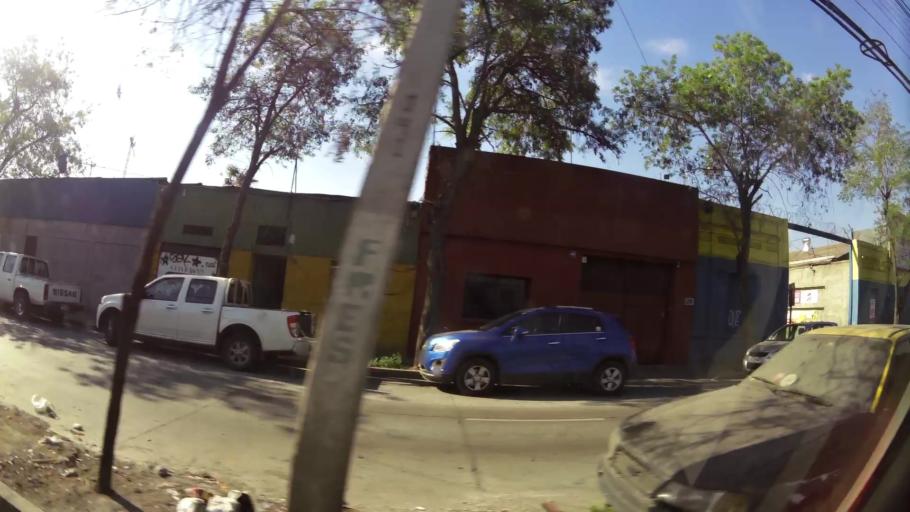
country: CL
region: Santiago Metropolitan
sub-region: Provincia de Santiago
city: Santiago
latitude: -33.4794
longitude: -70.6505
